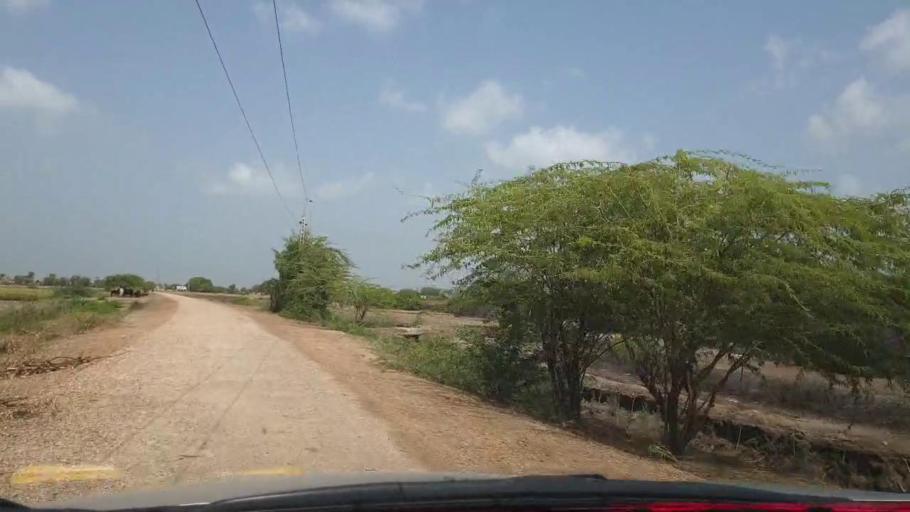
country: PK
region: Sindh
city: Rajo Khanani
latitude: 24.9270
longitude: 68.8990
